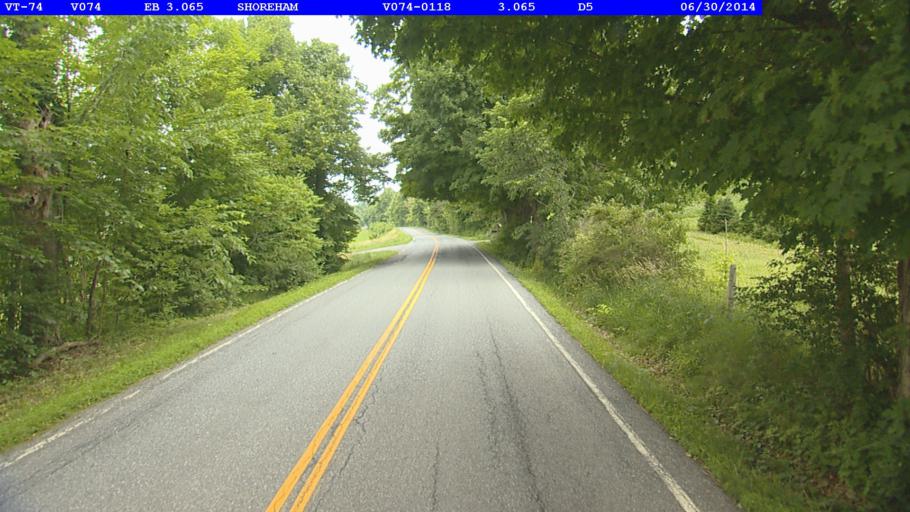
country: US
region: New York
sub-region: Essex County
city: Ticonderoga
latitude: 43.8760
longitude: -73.3332
